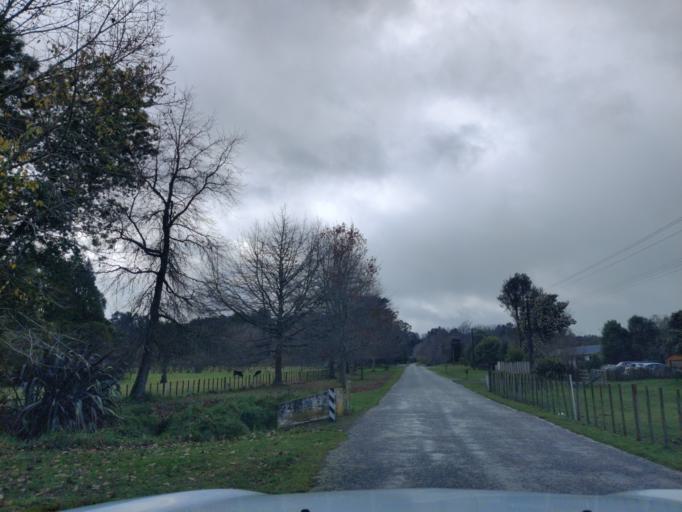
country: NZ
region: Manawatu-Wanganui
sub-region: Palmerston North City
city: Palmerston North
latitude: -40.1721
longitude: 175.7968
